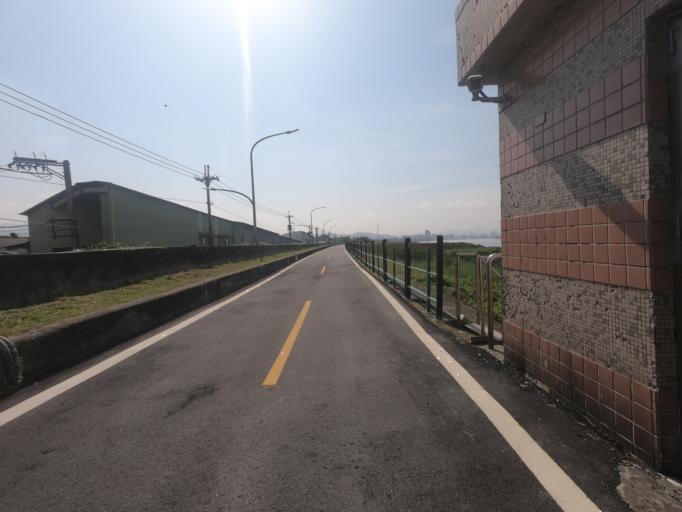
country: TW
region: Taipei
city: Taipei
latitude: 25.1039
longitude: 121.4806
